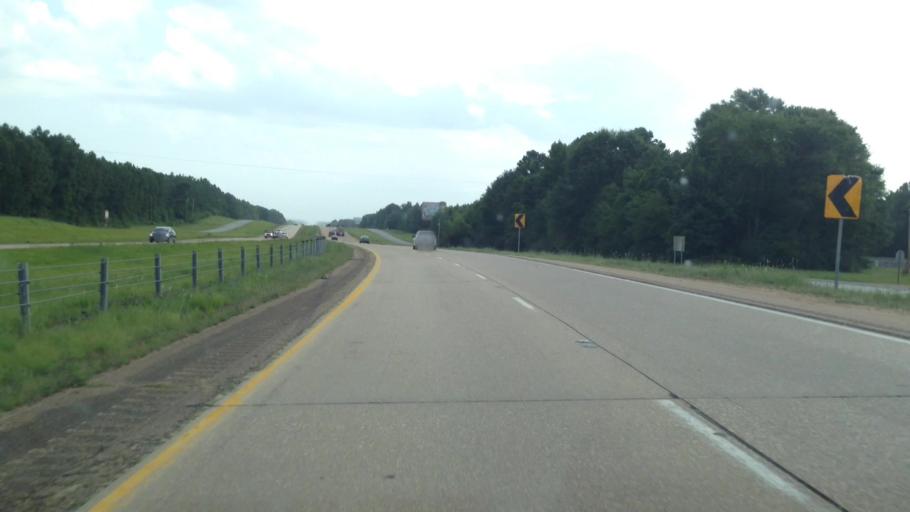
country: US
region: Mississippi
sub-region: Hinds County
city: Terry
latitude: 32.0677
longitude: -90.3198
